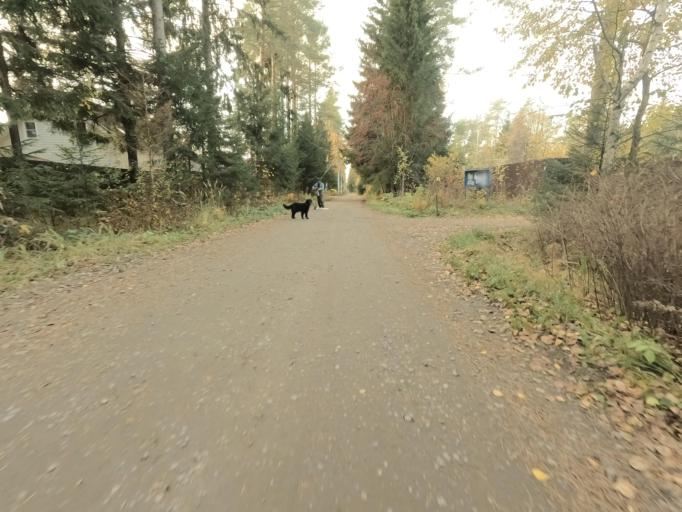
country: RU
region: St.-Petersburg
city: Beloostrov
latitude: 60.1668
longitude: 29.9917
